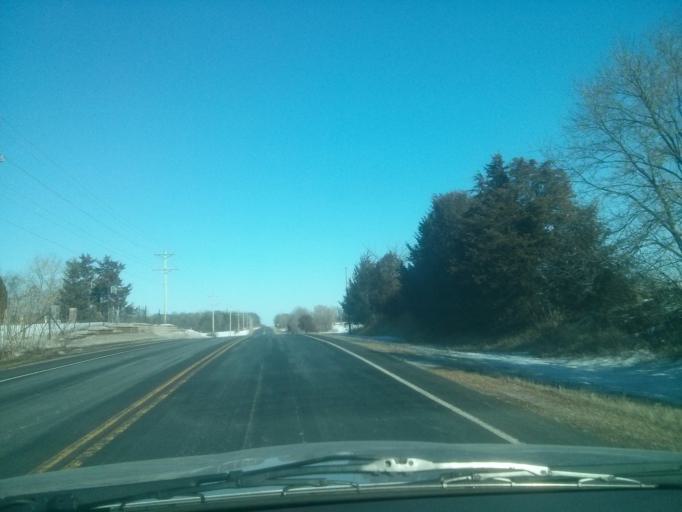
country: US
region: Minnesota
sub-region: Washington County
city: Bayport
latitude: 45.0744
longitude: -92.7361
